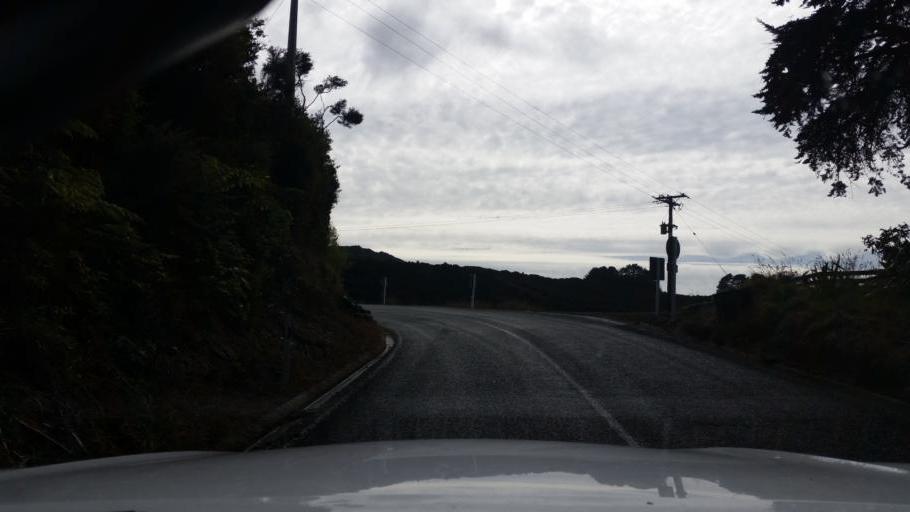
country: NZ
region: Auckland
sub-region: Auckland
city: Wellsford
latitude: -36.0869
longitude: 174.5357
